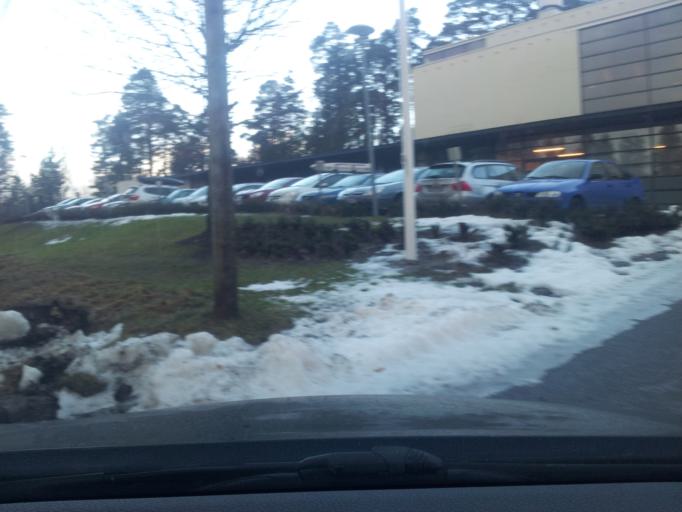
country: FI
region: Uusimaa
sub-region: Helsinki
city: Kirkkonummi
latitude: 60.1607
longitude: 24.5457
